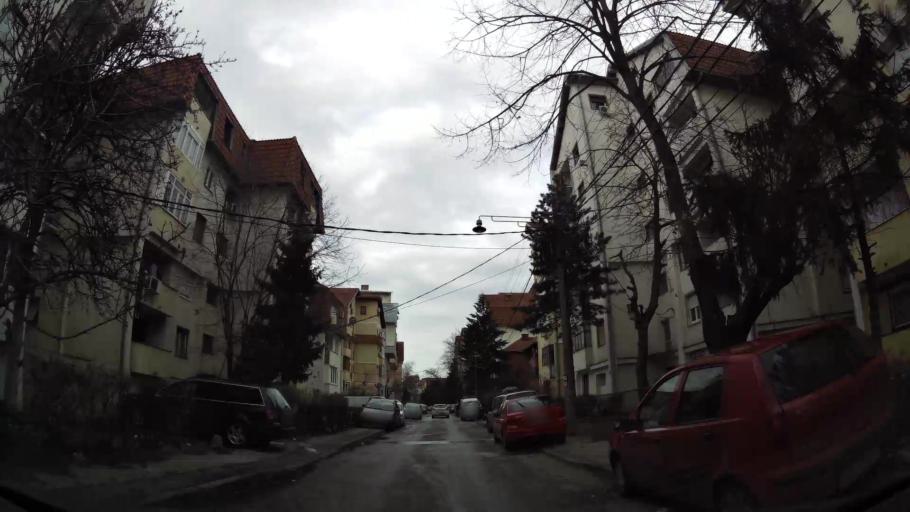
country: RS
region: Central Serbia
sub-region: Belgrade
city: Cukarica
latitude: 44.7527
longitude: 20.4098
